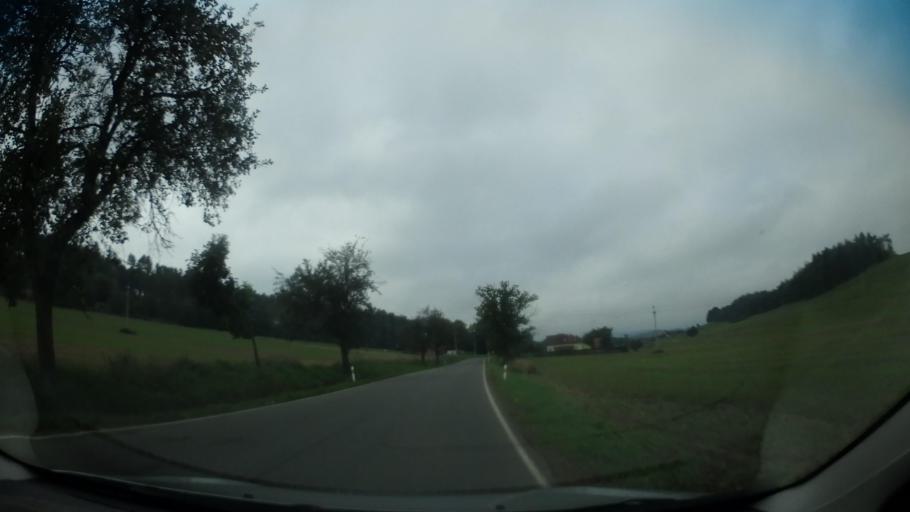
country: CZ
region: Central Bohemia
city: Neveklov
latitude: 49.7252
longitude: 14.4878
